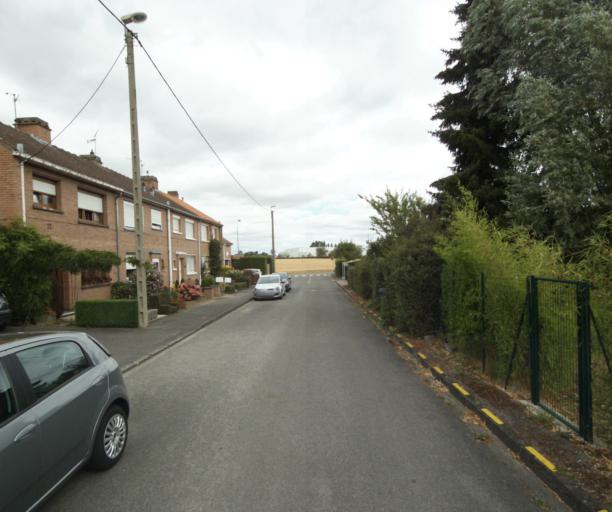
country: FR
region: Nord-Pas-de-Calais
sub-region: Departement du Nord
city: Linselles
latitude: 50.7436
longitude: 3.0842
